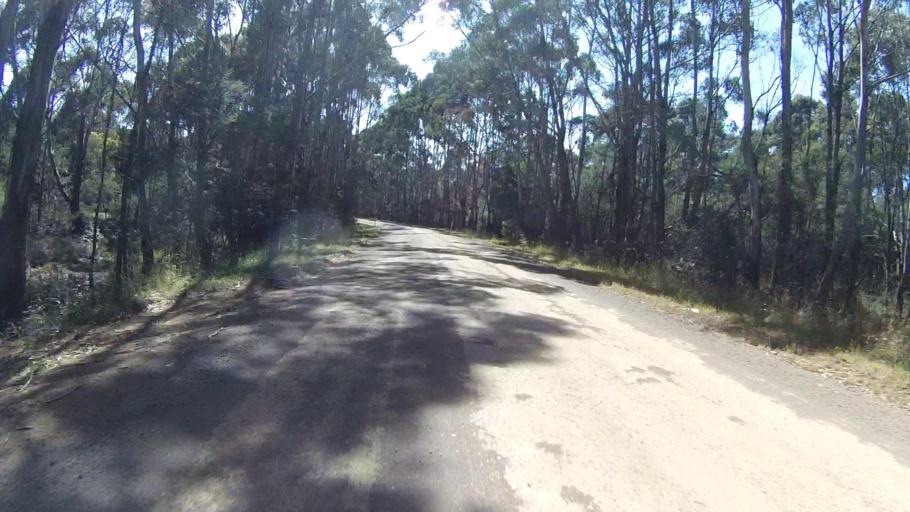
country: AU
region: Tasmania
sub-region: Sorell
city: Sorell
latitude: -42.7525
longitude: 147.6966
